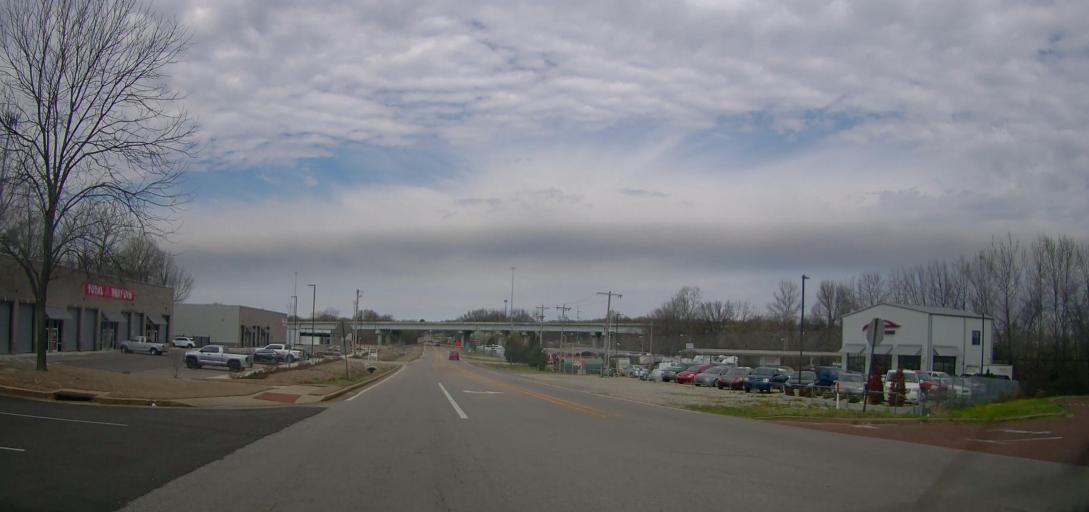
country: US
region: Mississippi
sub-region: De Soto County
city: Olive Branch
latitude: 34.9661
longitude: -89.8309
